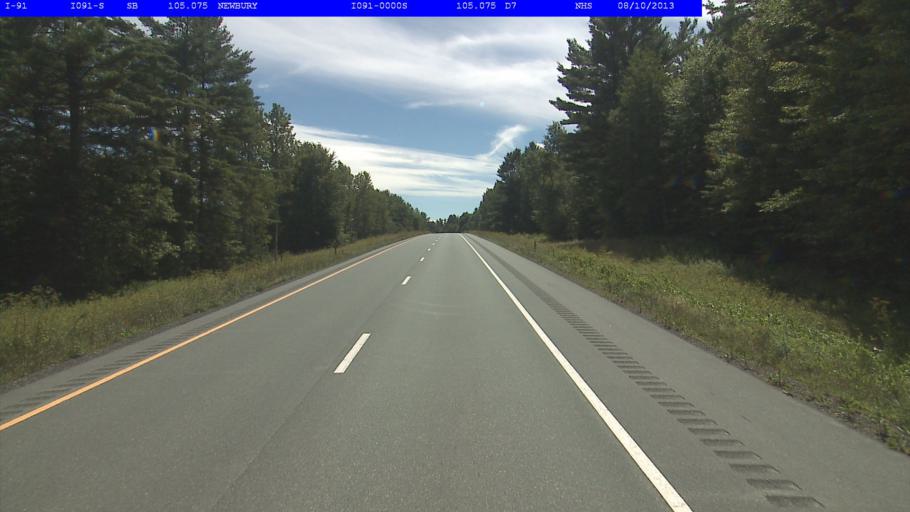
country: US
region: New Hampshire
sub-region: Grafton County
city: Haverhill
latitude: 44.0870
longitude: -72.1130
